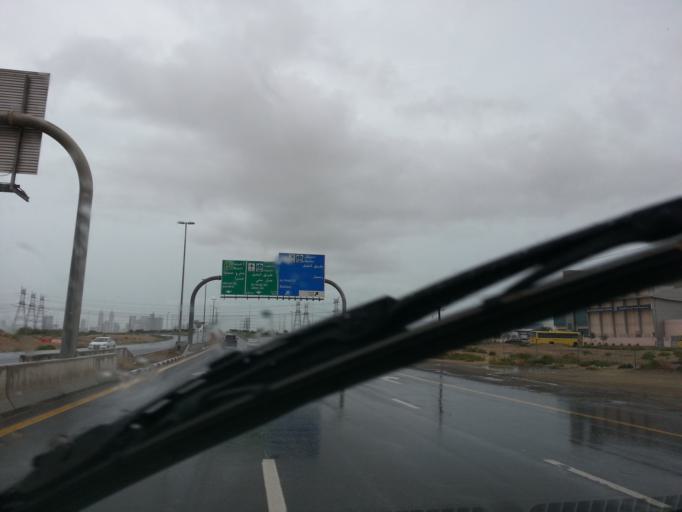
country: AE
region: Dubai
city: Dubai
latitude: 25.0728
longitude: 55.2153
